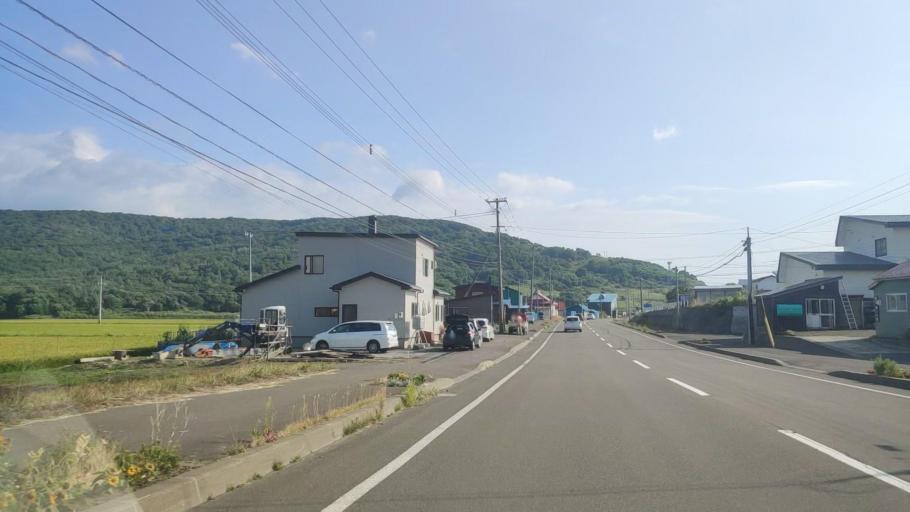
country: JP
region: Hokkaido
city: Ishikari
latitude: 43.5762
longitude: 141.3866
